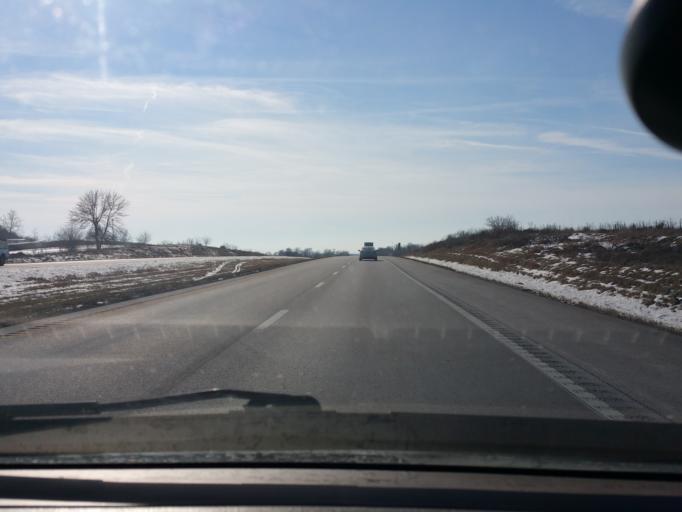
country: US
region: Missouri
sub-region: Clinton County
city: Cameron
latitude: 39.7989
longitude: -94.2012
